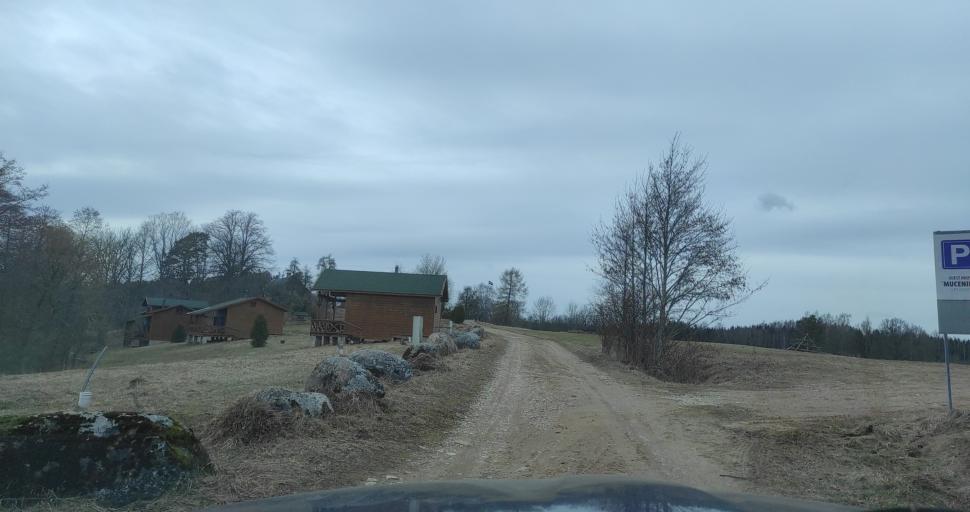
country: LV
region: Tukuma Rajons
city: Tukums
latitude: 57.0982
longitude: 23.0901
